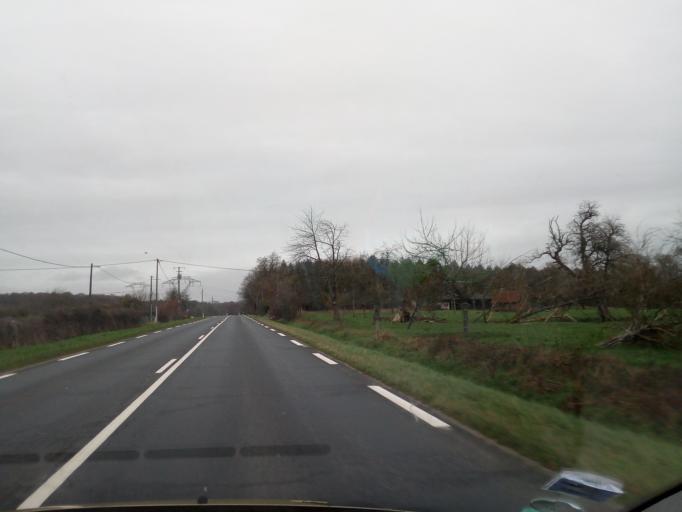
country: FR
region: Haute-Normandie
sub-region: Departement de l'Eure
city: Hauville
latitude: 49.4102
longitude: 0.7967
